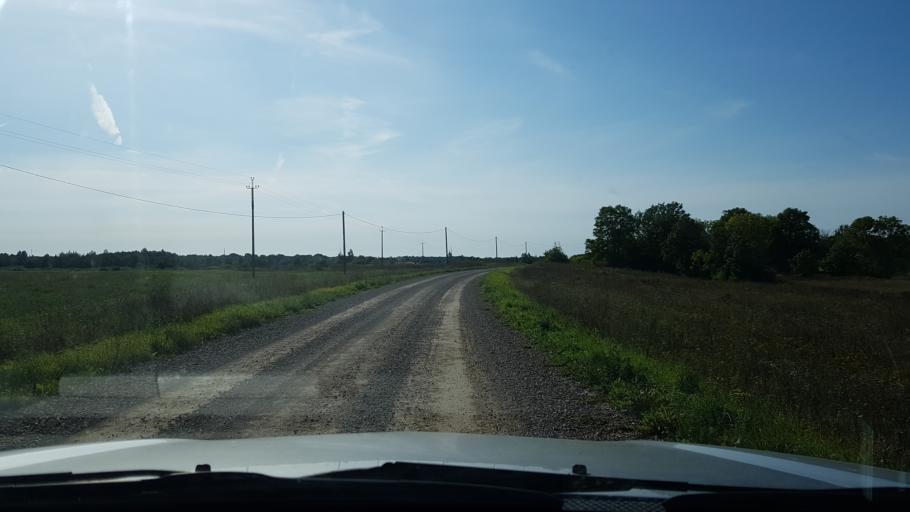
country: EE
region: Ida-Virumaa
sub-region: Narva-Joesuu linn
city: Narva-Joesuu
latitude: 59.4090
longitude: 28.0231
